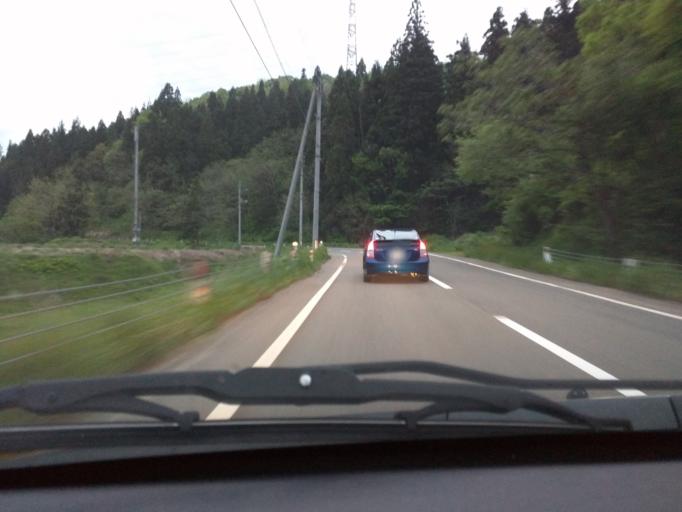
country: JP
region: Niigata
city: Ojiya
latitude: 37.3215
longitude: 138.6910
